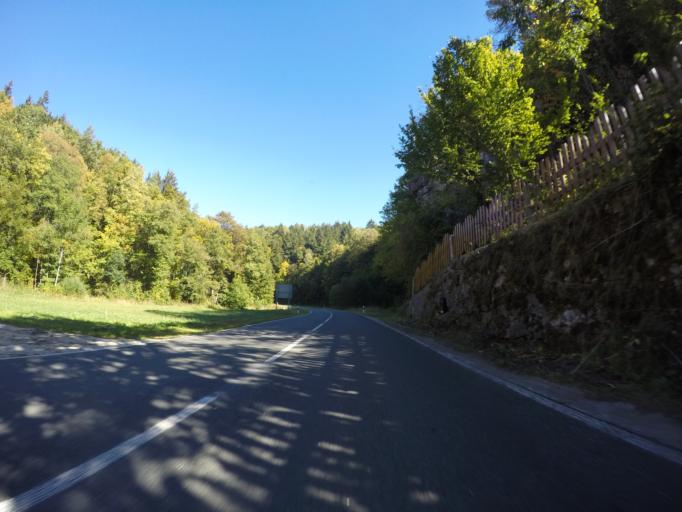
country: DE
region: Bavaria
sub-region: Upper Franconia
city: Waischenfeld
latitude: 49.8106
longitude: 11.3644
